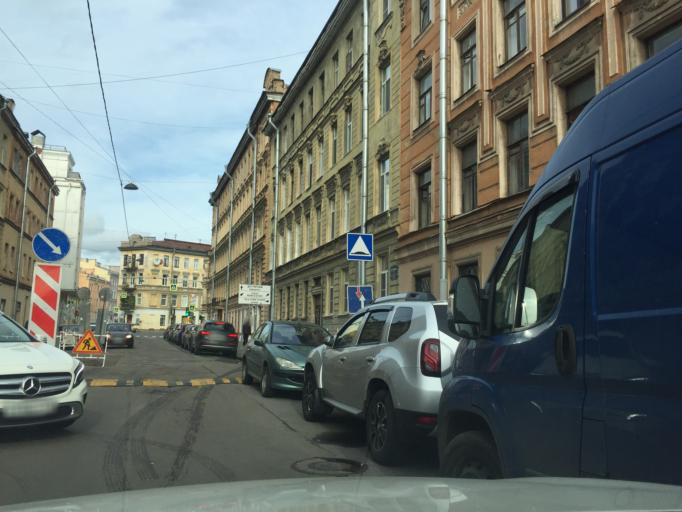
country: RU
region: St.-Petersburg
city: Centralniy
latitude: 59.9368
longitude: 30.3770
